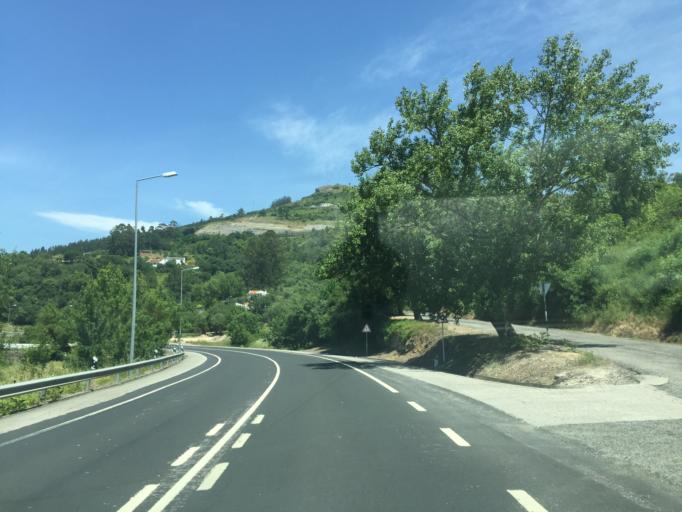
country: PT
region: Lisbon
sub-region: Mafra
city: Venda do Pinheiro
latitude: 38.8915
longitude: -9.2016
